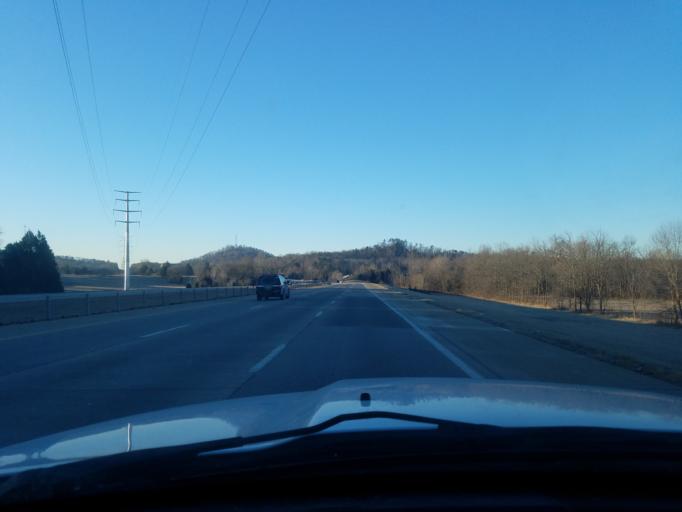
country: US
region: Kentucky
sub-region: Bullitt County
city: Lebanon Junction
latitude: 37.8534
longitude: -85.7112
